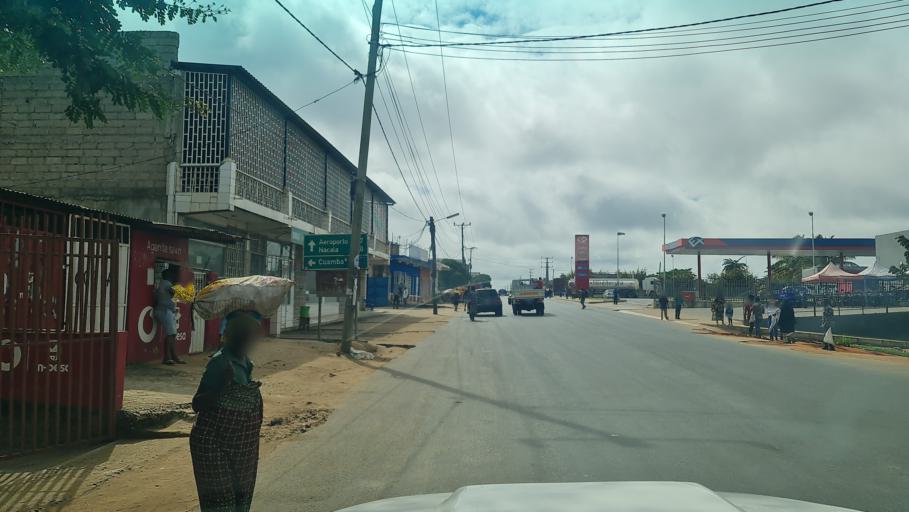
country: MZ
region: Nampula
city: Nampula
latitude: -15.1122
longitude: 39.2262
